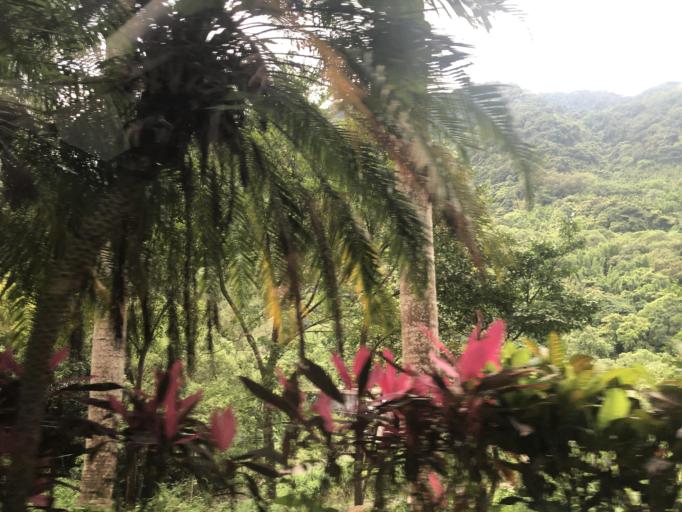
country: TW
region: Taiwan
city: Daxi
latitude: 24.8728
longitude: 121.4032
